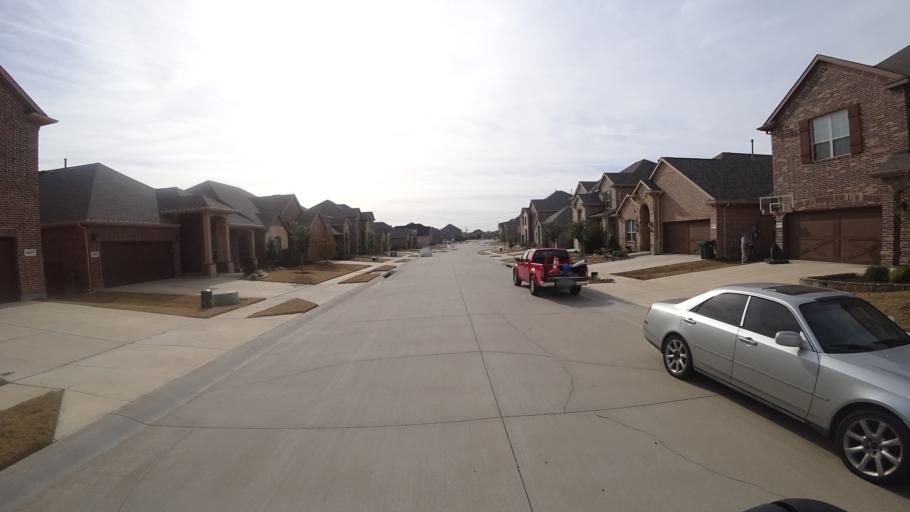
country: US
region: Texas
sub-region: Denton County
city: Highland Village
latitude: 33.0746
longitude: -97.0295
